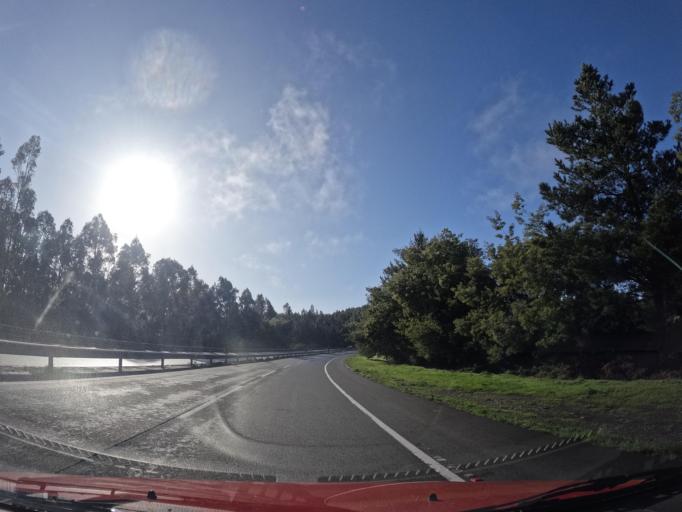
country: CL
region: Biobio
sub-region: Provincia de Concepcion
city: Penco
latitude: -36.7390
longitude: -72.9007
